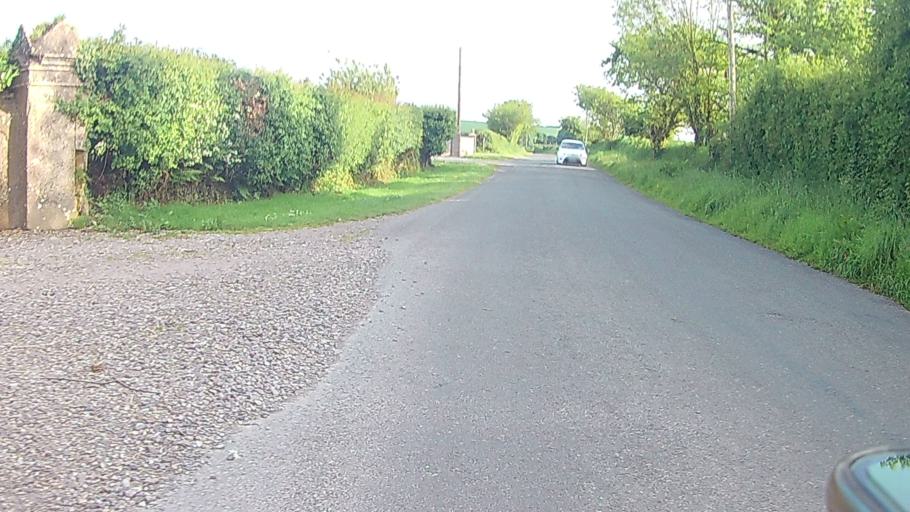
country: IE
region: Munster
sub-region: County Cork
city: Cork
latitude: 51.9842
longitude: -8.4578
